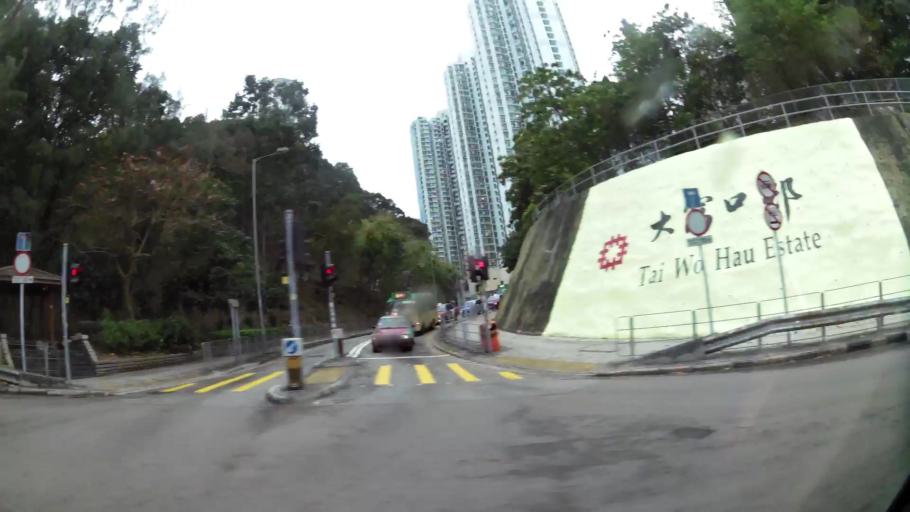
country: HK
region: Tsuen Wan
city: Tsuen Wan
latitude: 22.3665
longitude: 114.1250
